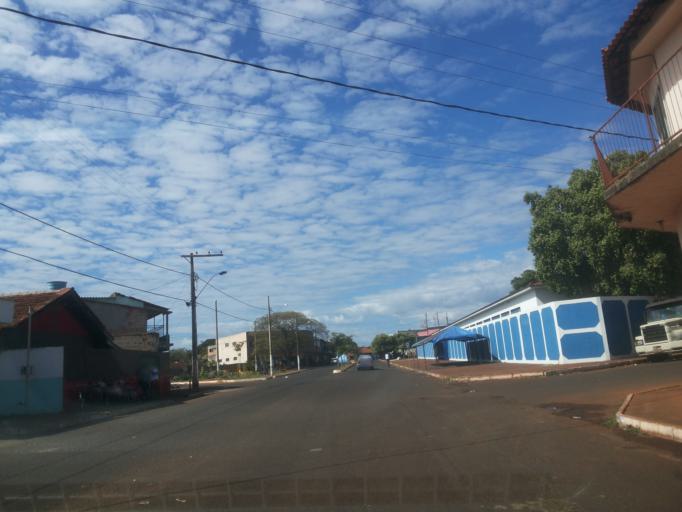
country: BR
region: Minas Gerais
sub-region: Centralina
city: Centralina
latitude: -18.5821
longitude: -49.2045
